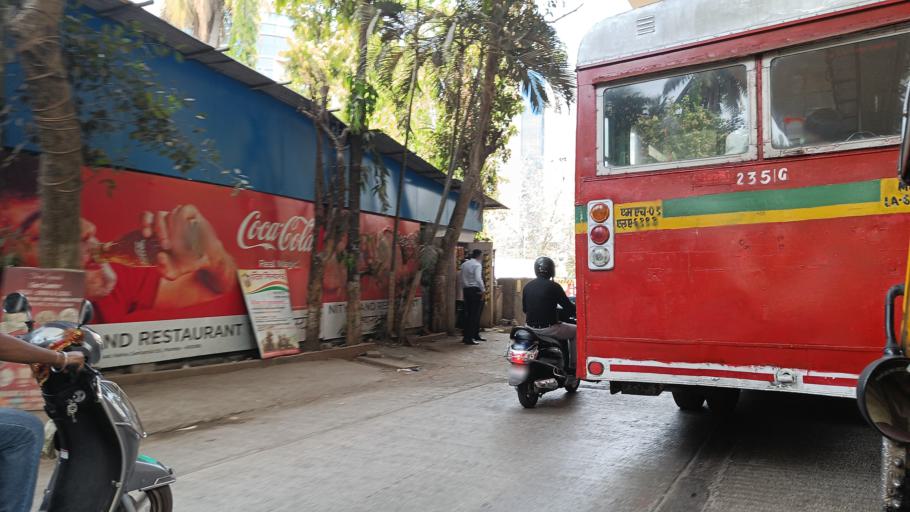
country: IN
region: Maharashtra
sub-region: Mumbai Suburban
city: Mumbai
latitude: 19.0728
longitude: 72.8645
